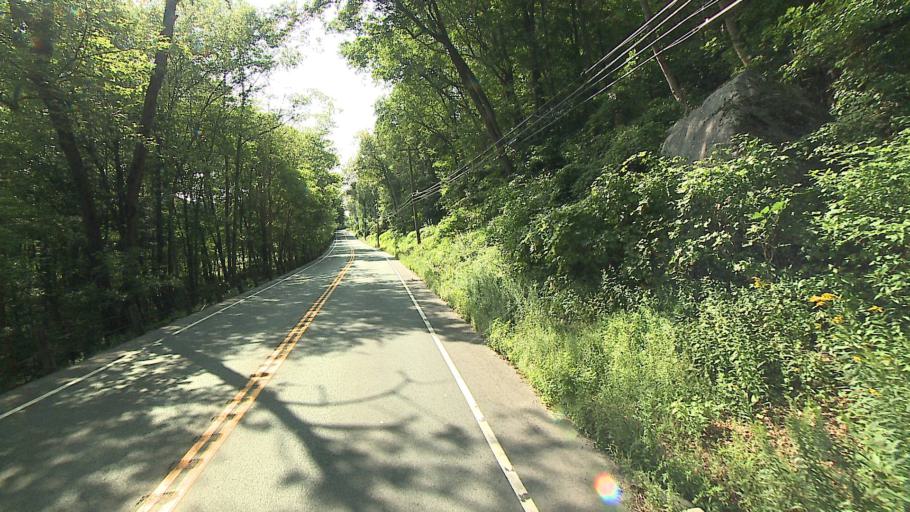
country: US
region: Connecticut
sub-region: Fairfield County
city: Sherman
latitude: 41.6313
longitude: -73.4708
